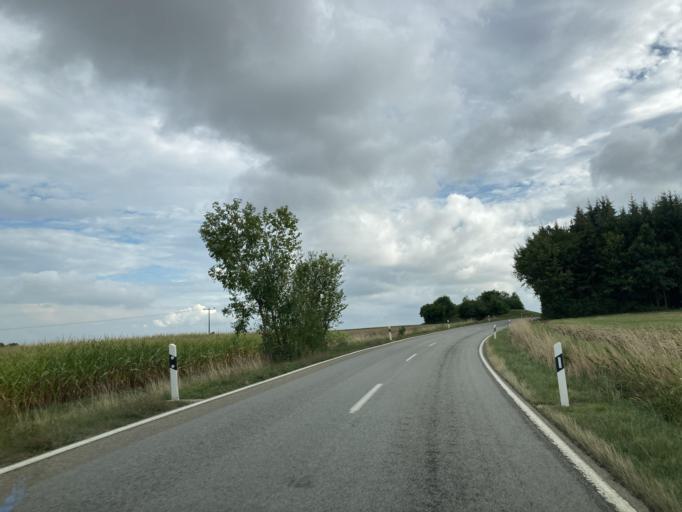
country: DE
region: Bavaria
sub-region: Swabia
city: Forheim
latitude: 48.7435
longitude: 10.4040
